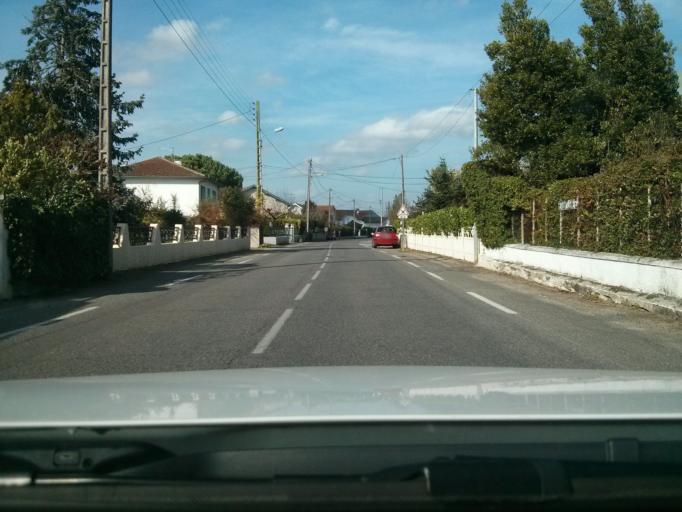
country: FR
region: Midi-Pyrenees
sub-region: Departement du Tarn-et-Garonne
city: Montbeton
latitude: 44.0130
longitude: 1.3227
